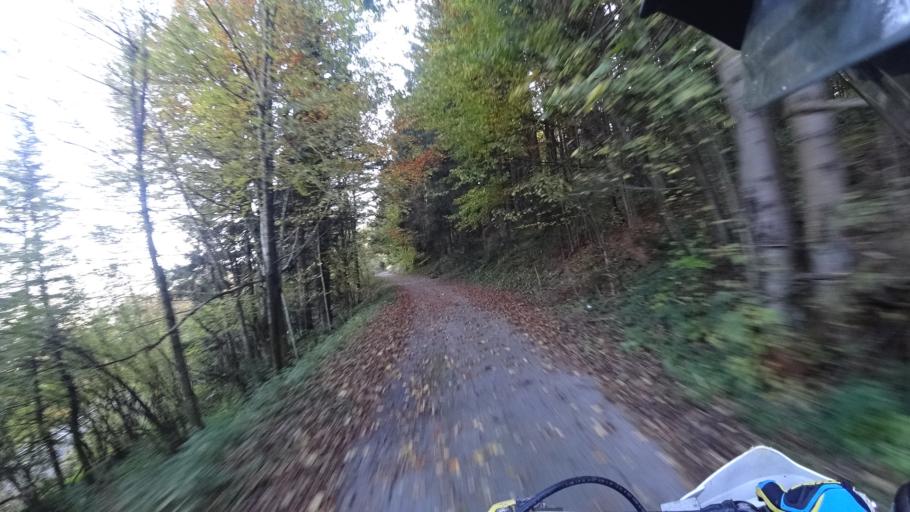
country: HR
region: Karlovacka
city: Plaski
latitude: 44.9825
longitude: 15.4231
